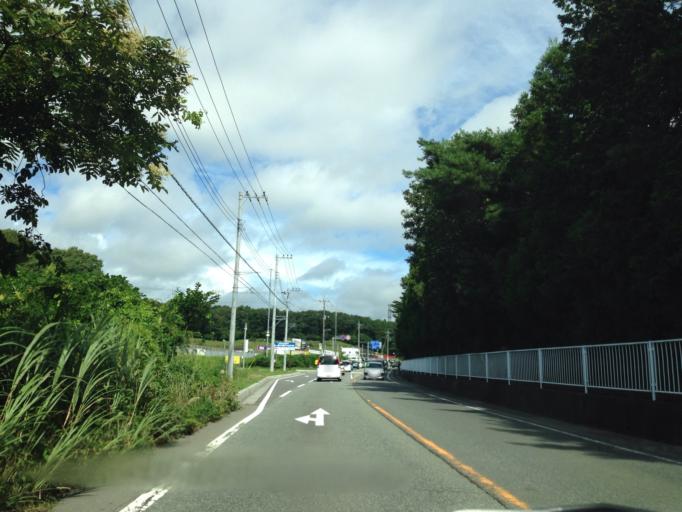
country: JP
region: Shizuoka
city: Gotemba
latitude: 35.3459
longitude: 138.8808
